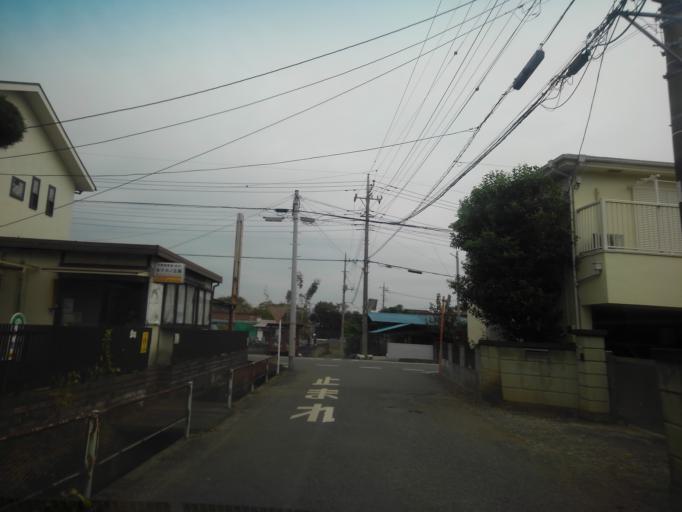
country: JP
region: Saitama
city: Sayama
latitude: 35.7911
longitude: 139.3765
